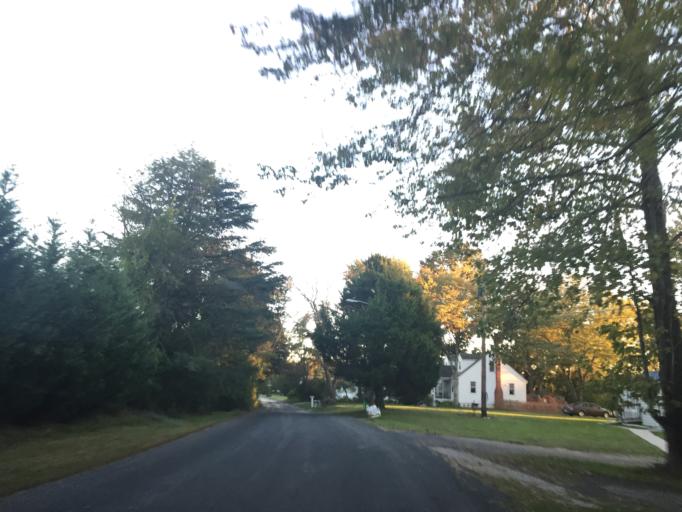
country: US
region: Maryland
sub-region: Baltimore County
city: Kingsville
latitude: 39.4230
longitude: -76.3937
